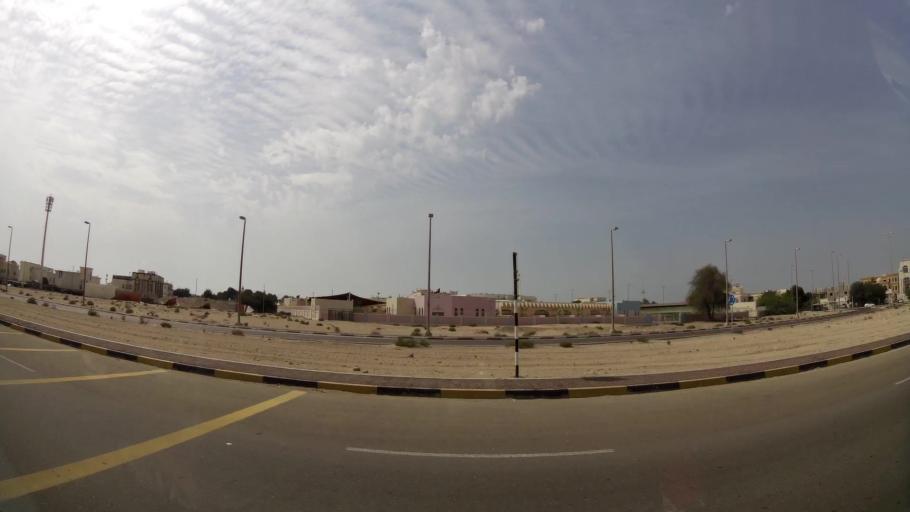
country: AE
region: Abu Dhabi
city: Abu Dhabi
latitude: 24.5541
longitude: 54.6852
